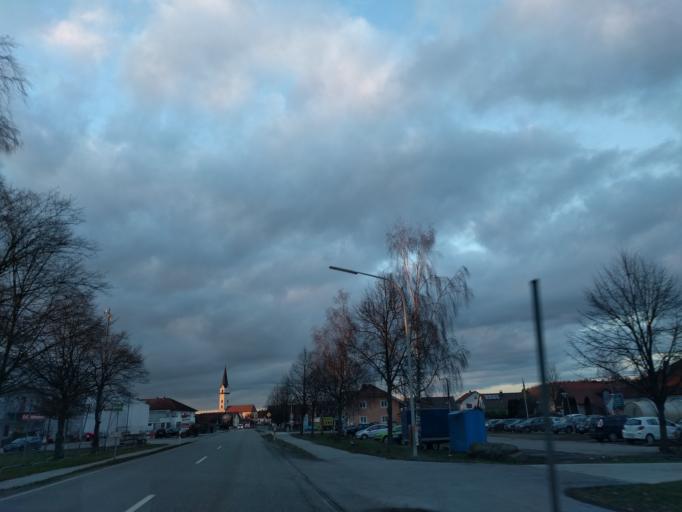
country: DE
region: Bavaria
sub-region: Lower Bavaria
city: Hofkirchen
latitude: 48.6741
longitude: 13.1217
